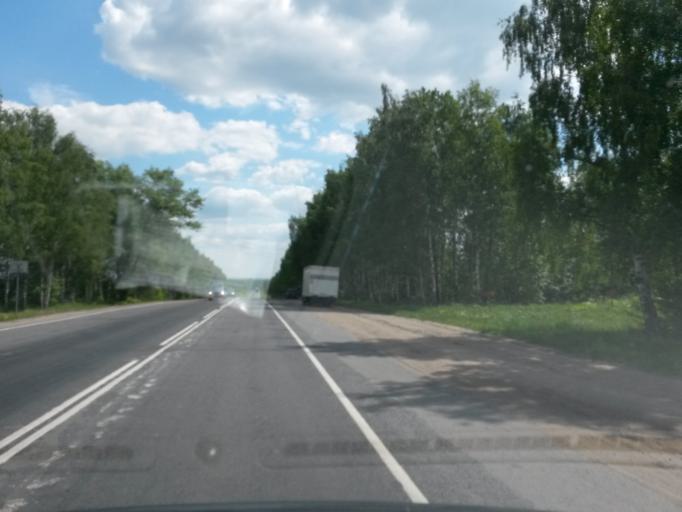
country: RU
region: Jaroslavl
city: Yaroslavl
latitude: 57.5586
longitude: 39.8583
